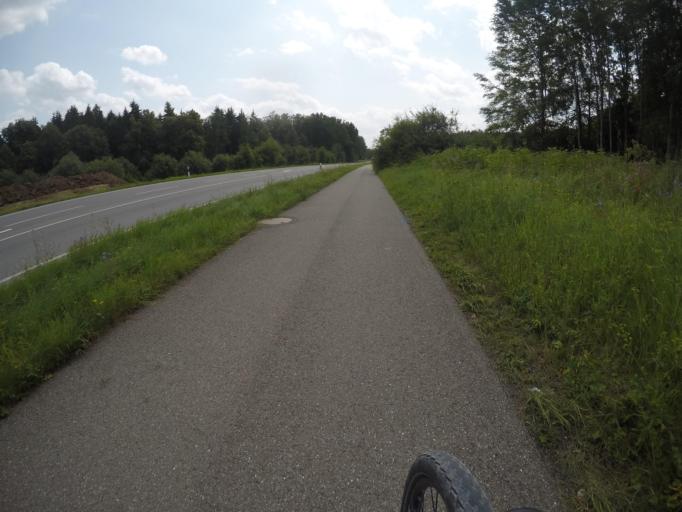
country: DE
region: Baden-Wuerttemberg
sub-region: Freiburg Region
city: Zimmern ob Rottweil
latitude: 48.1849
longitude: 8.6077
